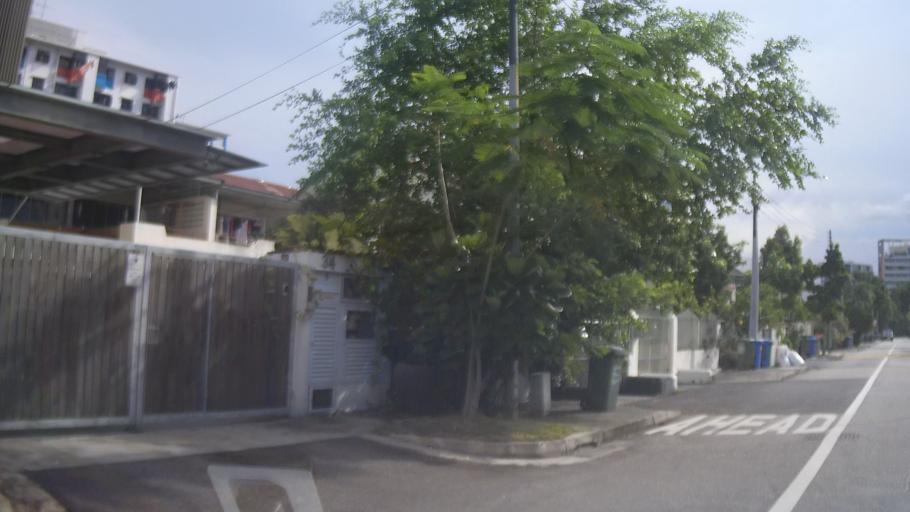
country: SG
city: Singapore
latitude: 1.3285
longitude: 103.8842
